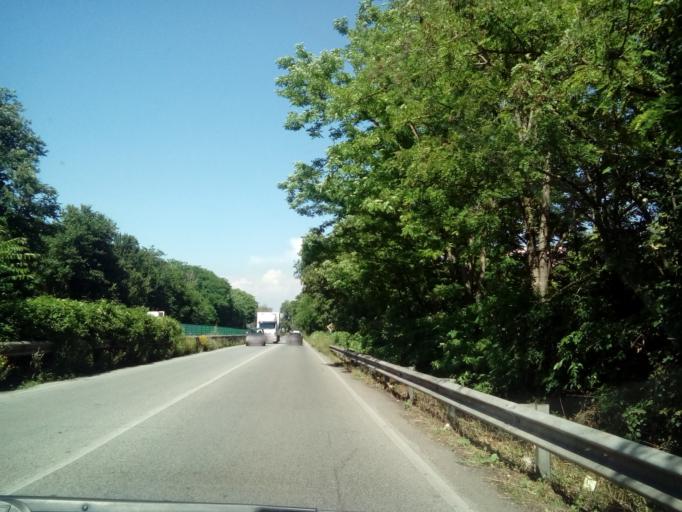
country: IT
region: Latium
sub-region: Citta metropolitana di Roma Capitale
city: Vitinia
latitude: 41.8331
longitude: 12.4541
